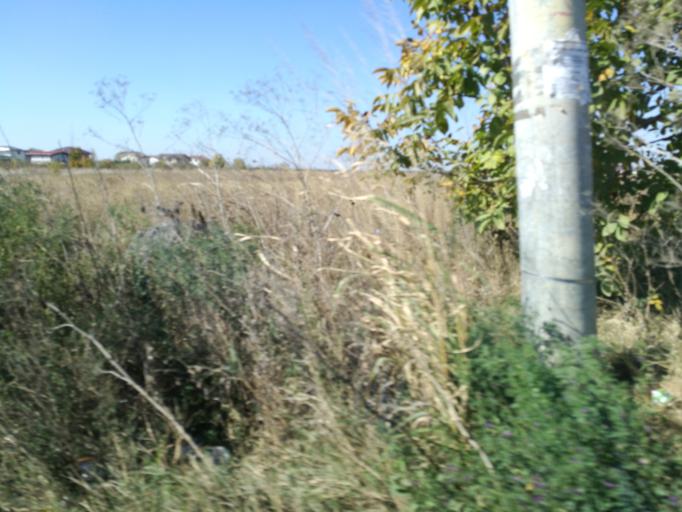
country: RO
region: Giurgiu
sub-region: Comuna Joita
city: Bacu
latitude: 44.4709
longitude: 25.8862
